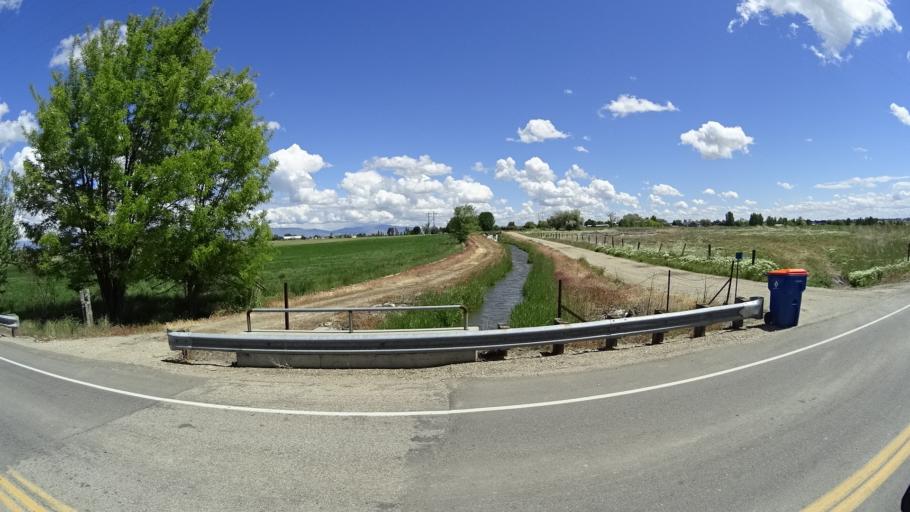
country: US
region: Idaho
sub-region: Ada County
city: Meridian
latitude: 43.5683
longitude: -116.4536
